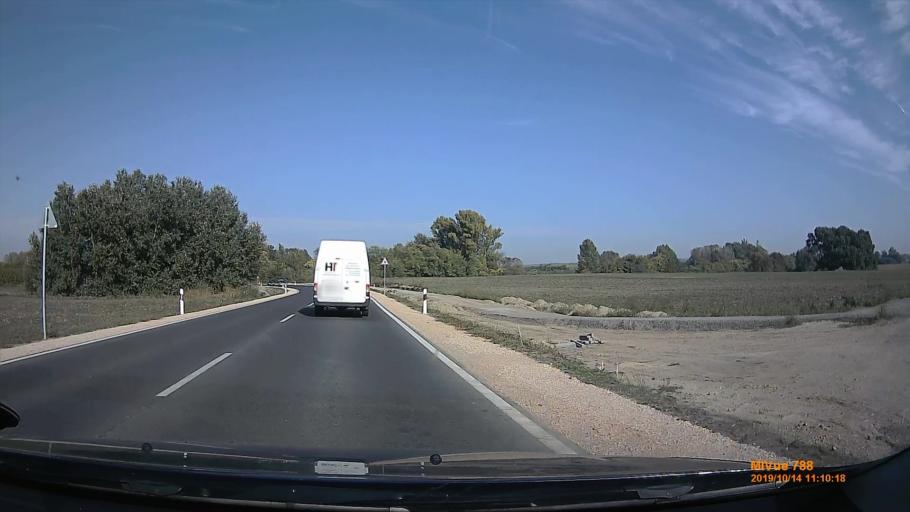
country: HU
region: Pest
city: Peteri
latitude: 47.3741
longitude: 19.4220
